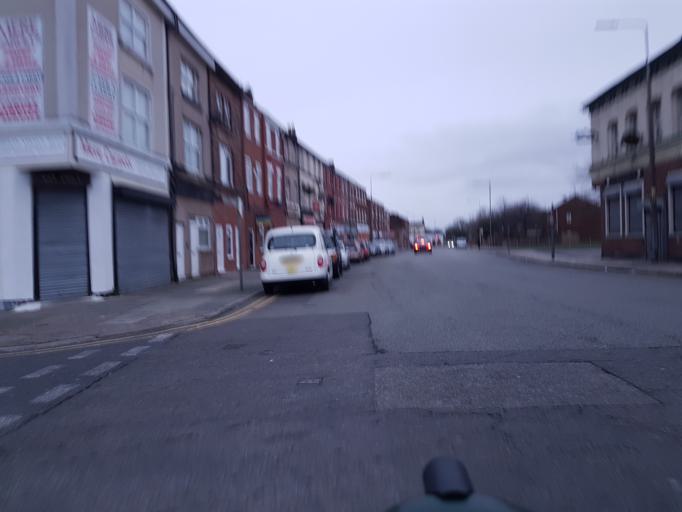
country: GB
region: England
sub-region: Liverpool
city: Liverpool
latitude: 53.4238
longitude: -2.9619
